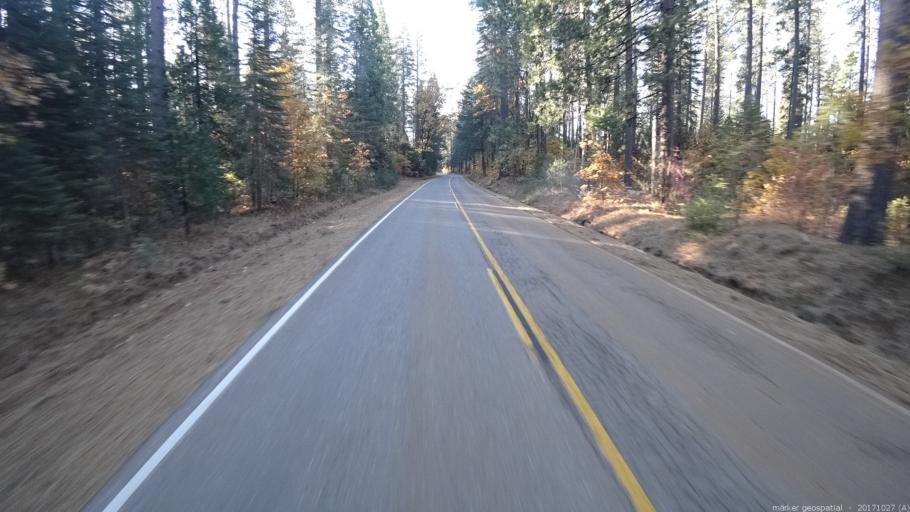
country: US
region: California
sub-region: Shasta County
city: Burney
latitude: 40.9363
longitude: -121.9487
